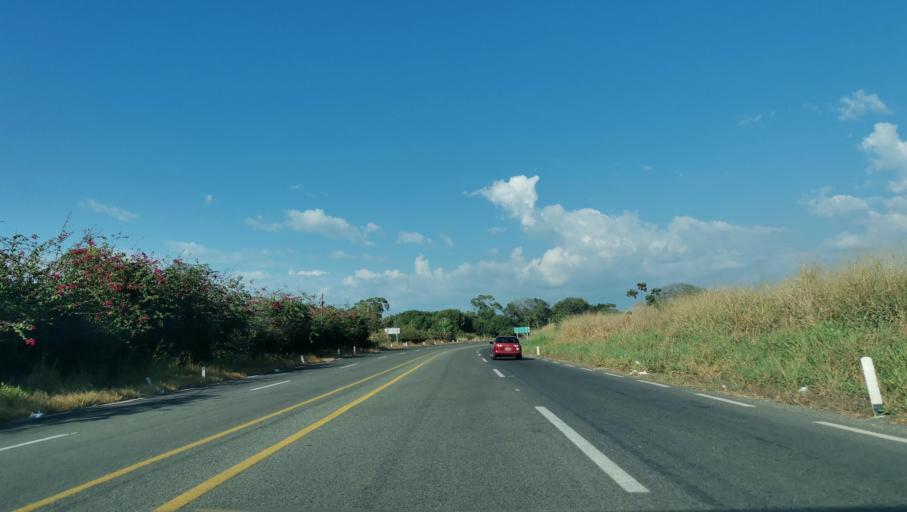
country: MX
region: Chiapas
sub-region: Tapachula
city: Congregacion Reforma
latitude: 14.8144
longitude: -92.3445
